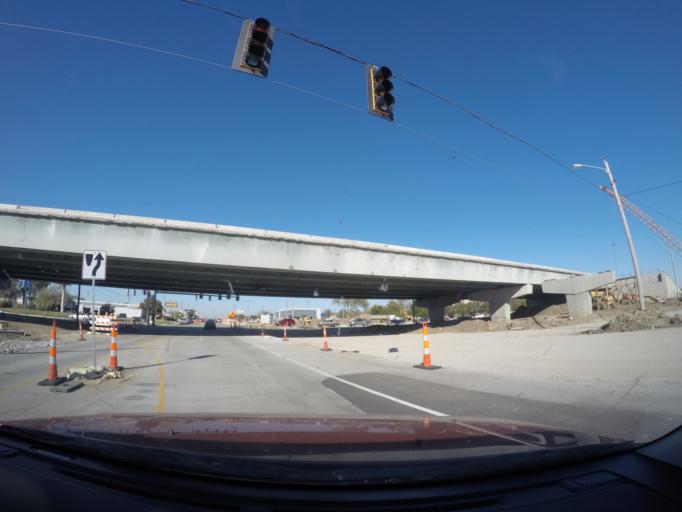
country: US
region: Kansas
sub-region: Sedgwick County
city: Wichita
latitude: 37.6733
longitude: -97.3894
